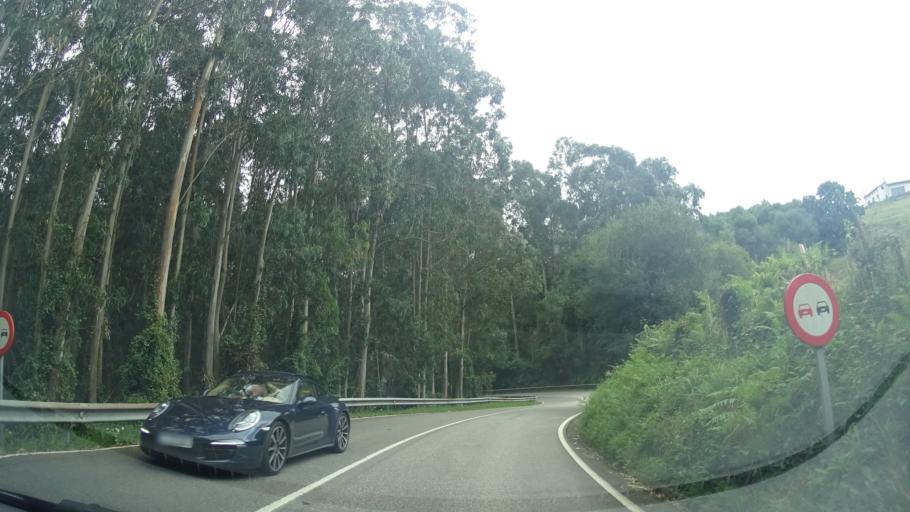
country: ES
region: Asturias
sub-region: Province of Asturias
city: Ribadesella
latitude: 43.4637
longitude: -5.0919
